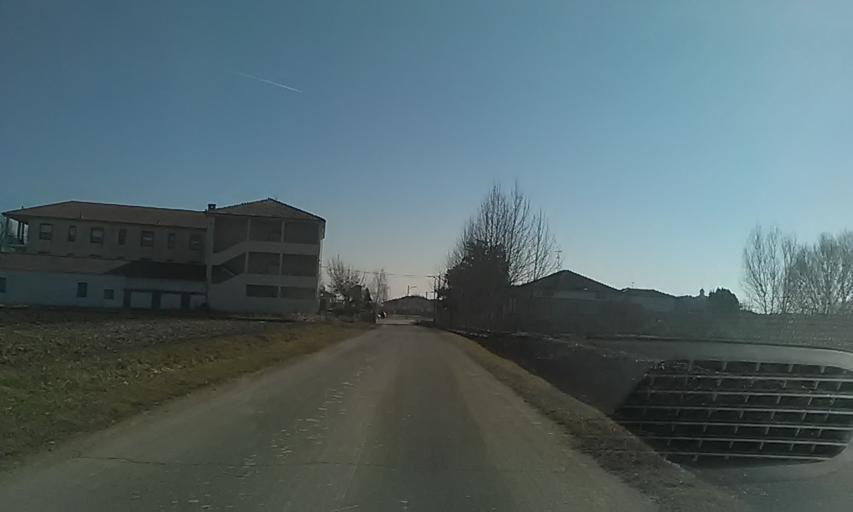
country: IT
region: Piedmont
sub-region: Provincia di Vercelli
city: San Germano Vercellese
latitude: 45.3555
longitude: 8.2465
